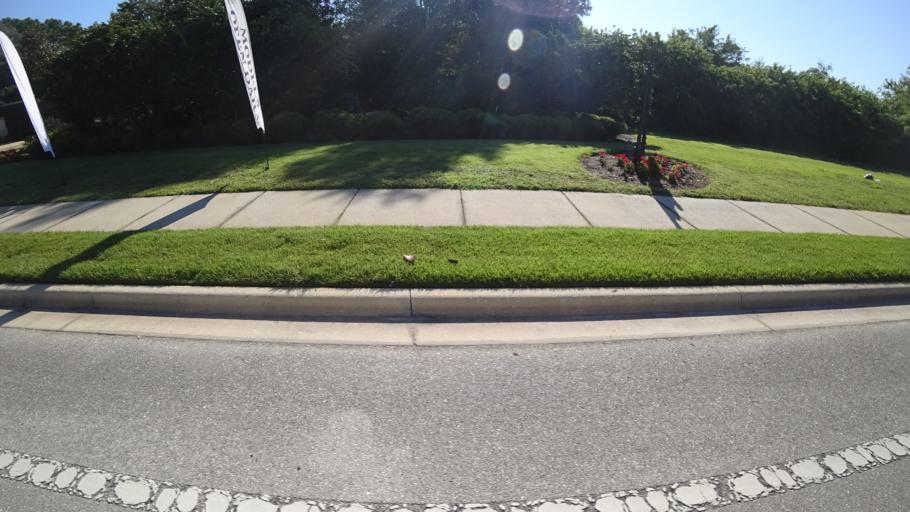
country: US
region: Florida
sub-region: Sarasota County
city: The Meadows
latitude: 27.3888
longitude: -82.3529
